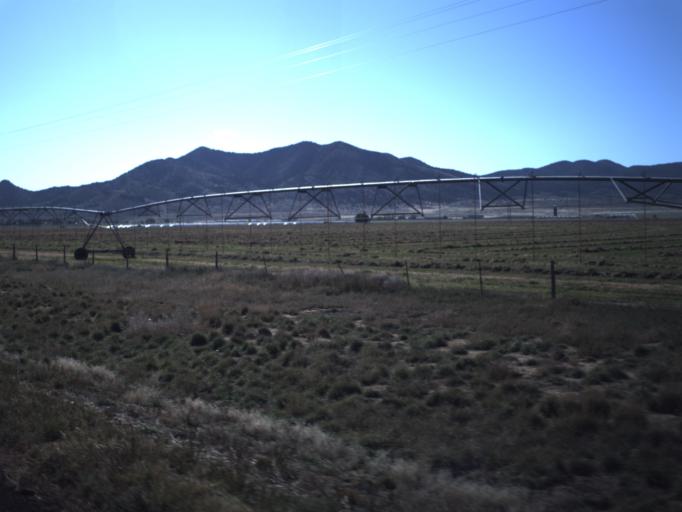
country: US
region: Utah
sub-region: Washington County
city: Enterprise
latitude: 37.6788
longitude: -113.5710
